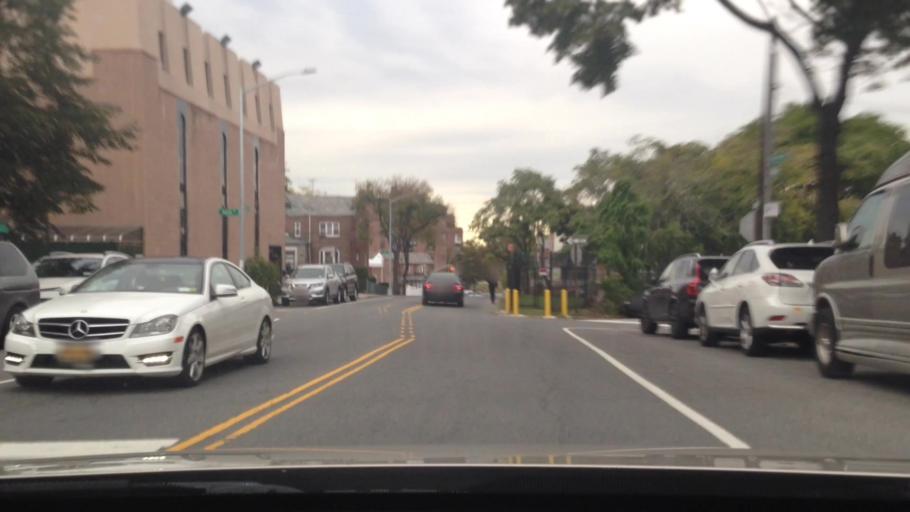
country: US
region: New York
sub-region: Queens County
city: Borough of Queens
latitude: 40.7337
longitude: -73.8525
